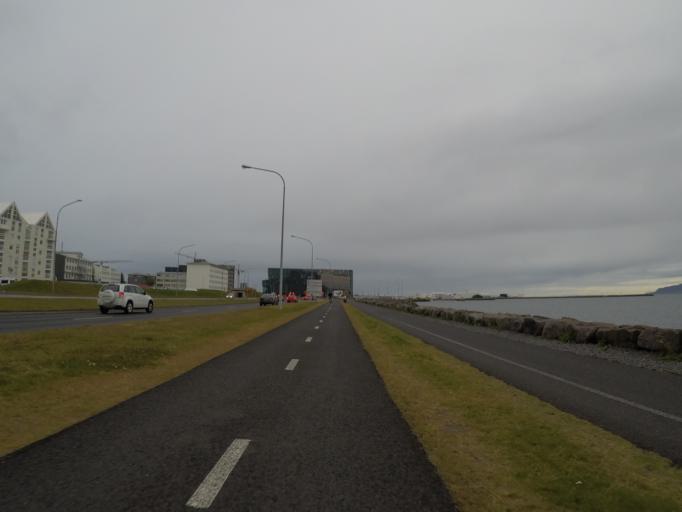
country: IS
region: Capital Region
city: Reykjavik
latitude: 64.1481
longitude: -21.9245
